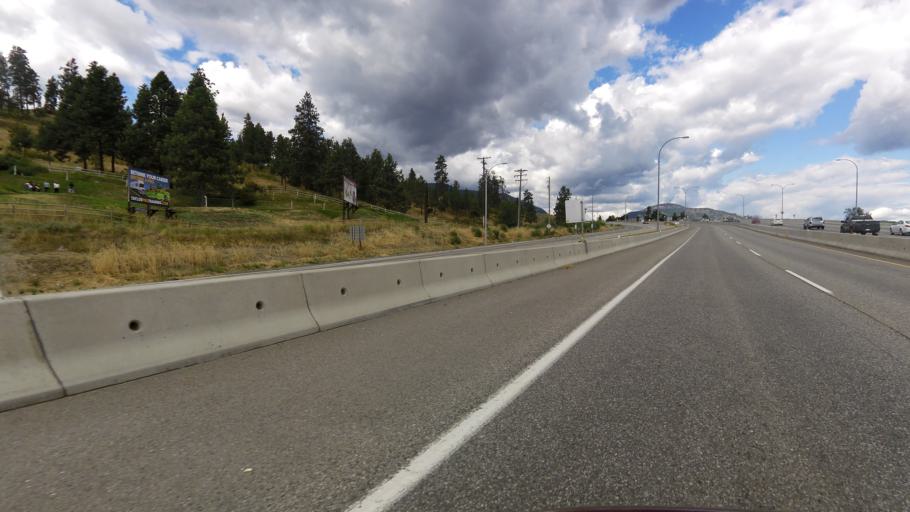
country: CA
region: British Columbia
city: Kelowna
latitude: 49.8799
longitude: -119.5242
